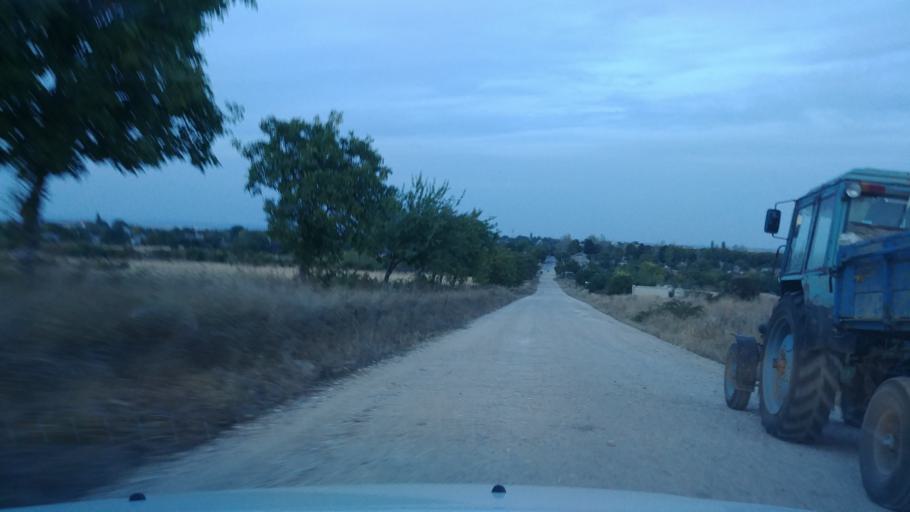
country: MD
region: Rezina
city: Saharna
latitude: 47.6702
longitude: 28.9482
